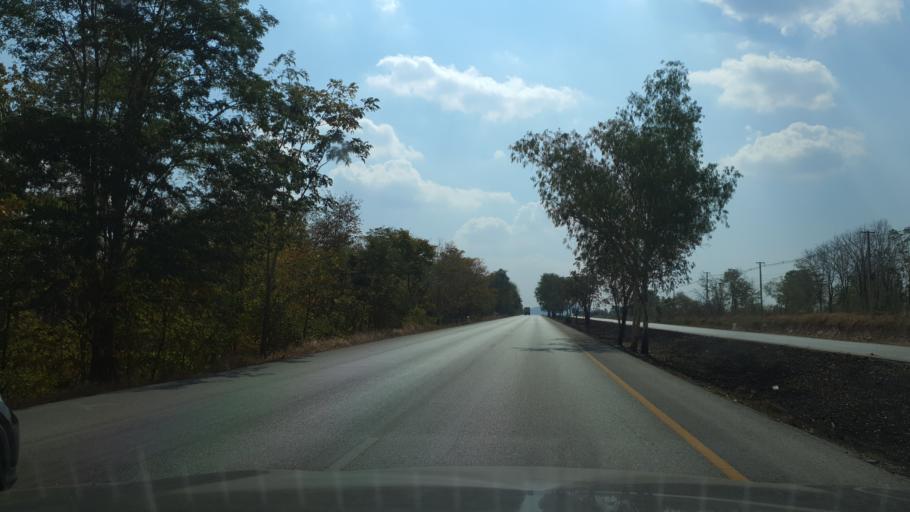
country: TH
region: Lampang
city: Mae Phrik
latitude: 17.3910
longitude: 99.1488
